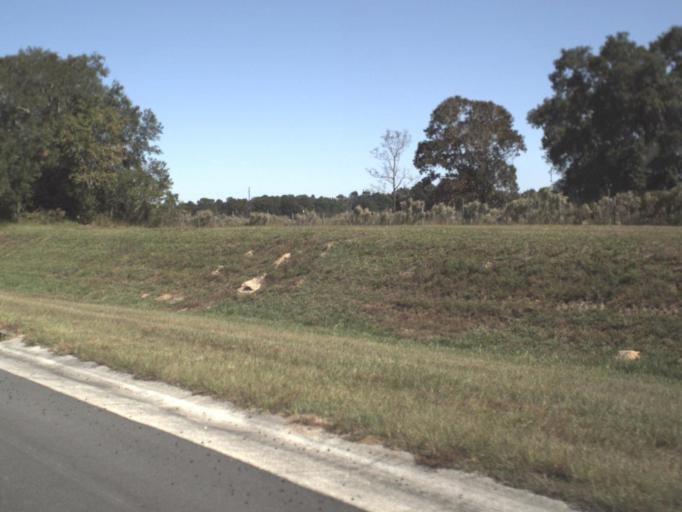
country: US
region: Florida
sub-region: Hernando County
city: Brookridge
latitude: 28.6211
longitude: -82.4931
